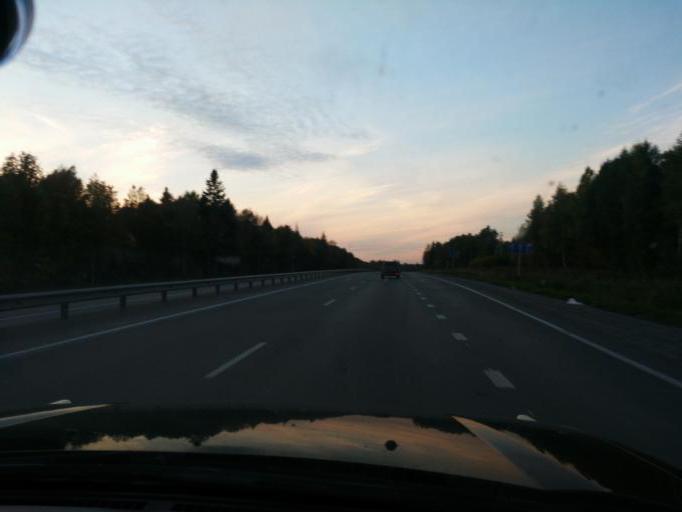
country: RU
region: Perm
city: Polazna
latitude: 58.2416
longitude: 56.4189
